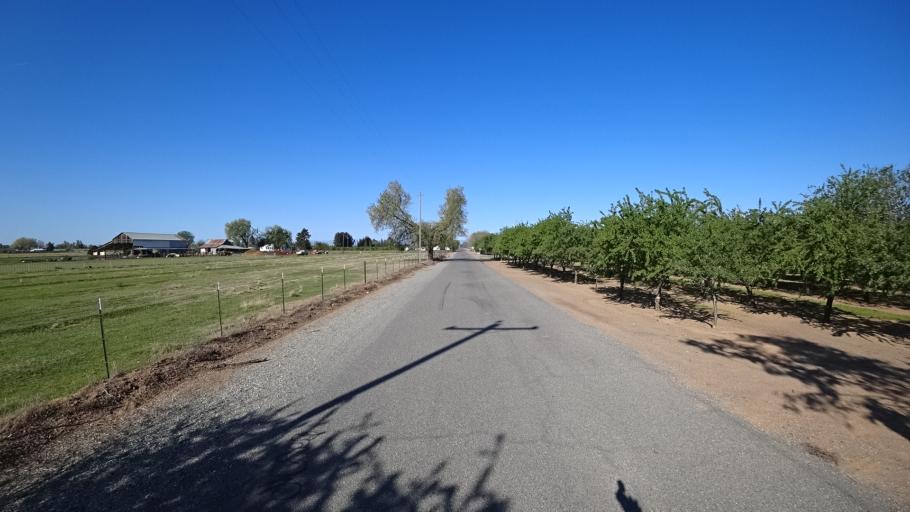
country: US
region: California
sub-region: Glenn County
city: Hamilton City
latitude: 39.7969
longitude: -122.0632
